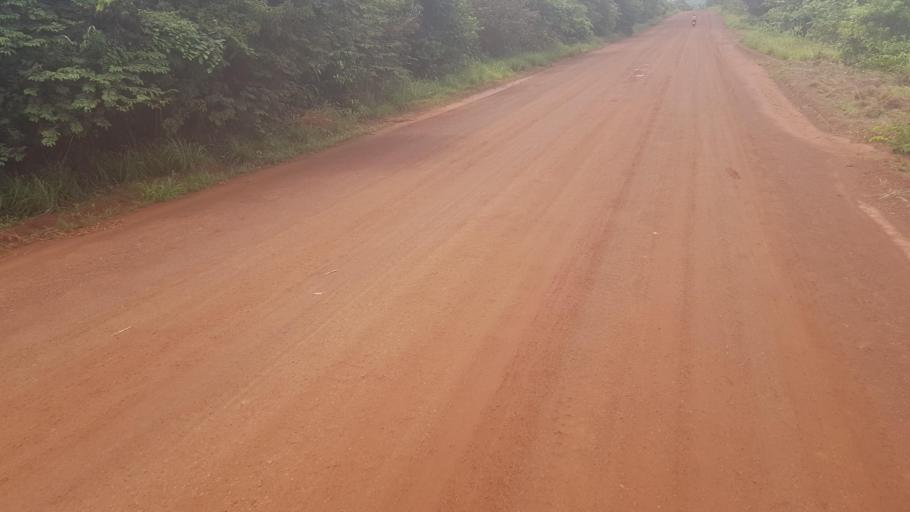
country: SL
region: Southern Province
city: Mogbwemo
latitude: 7.7491
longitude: -12.3052
